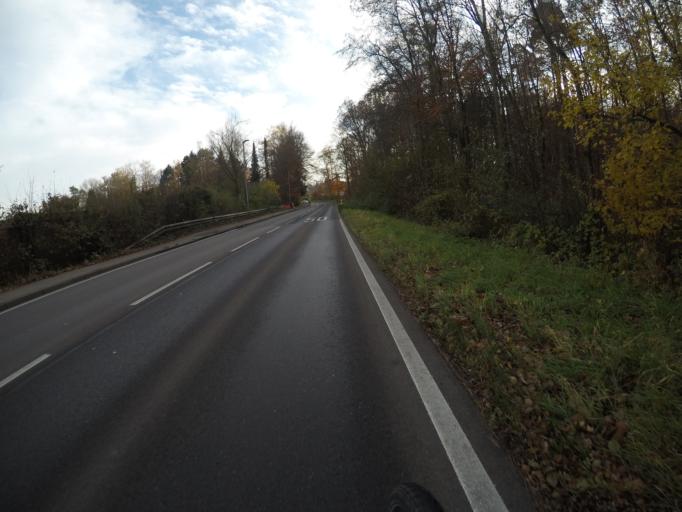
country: DE
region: Baden-Wuerttemberg
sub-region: Regierungsbezirk Stuttgart
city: Steinenbronn
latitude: 48.7080
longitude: 9.1097
